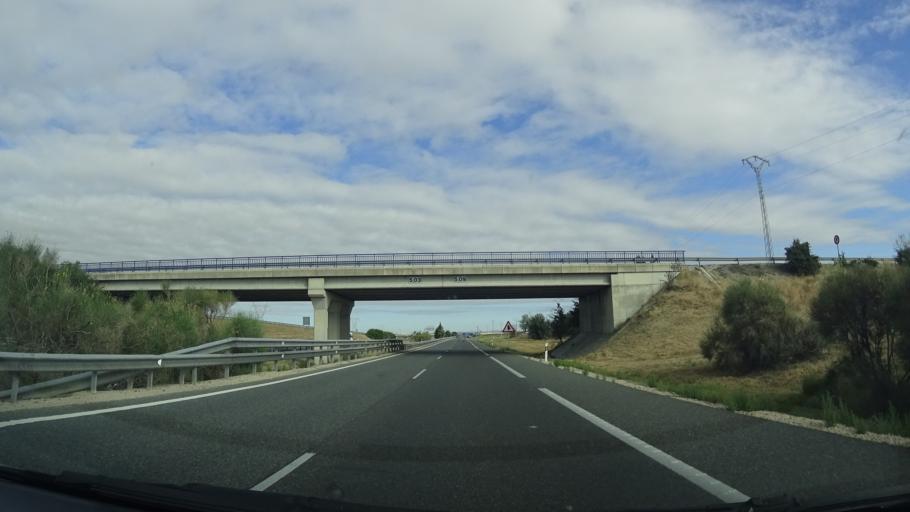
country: ES
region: Castille and Leon
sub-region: Provincia de Valladolid
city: San Vicente del Palacio
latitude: 41.2213
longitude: -4.8433
